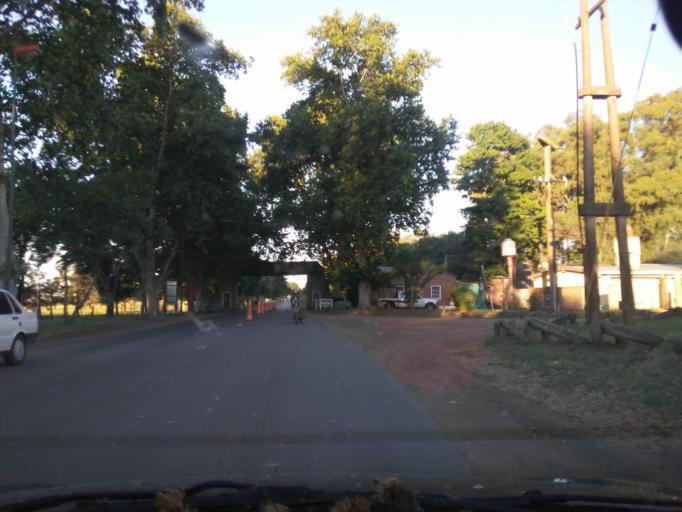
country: AR
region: Buenos Aires
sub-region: Partido de Junin
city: Junin
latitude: -34.6569
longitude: -61.0212
